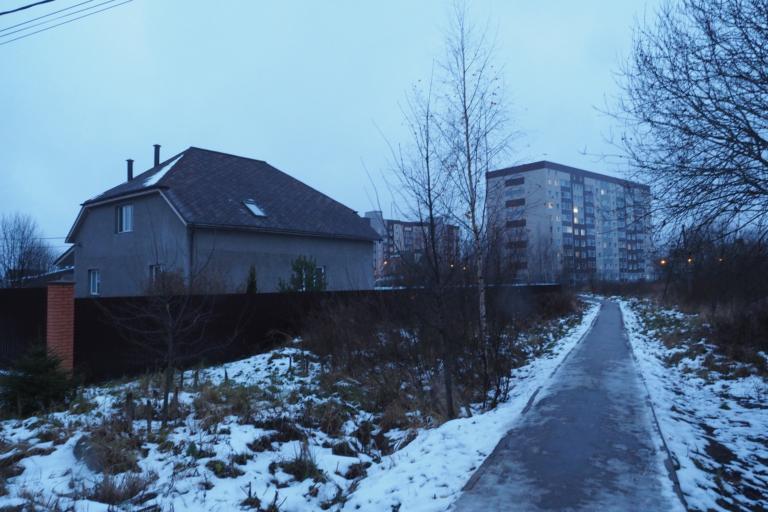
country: RU
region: Moskovskaya
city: Sergiyev Posad
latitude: 56.3368
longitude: 38.1391
